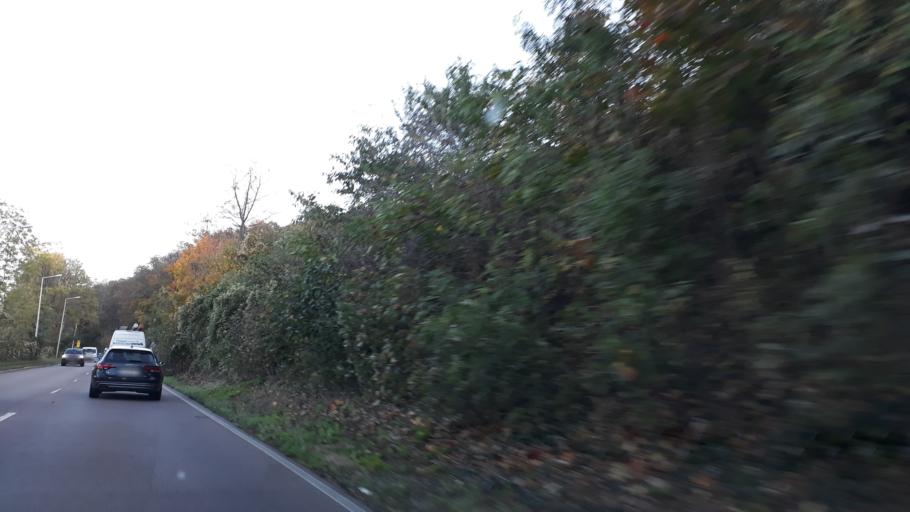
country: DE
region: Saxony
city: Coswig
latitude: 51.0893
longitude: 13.6116
